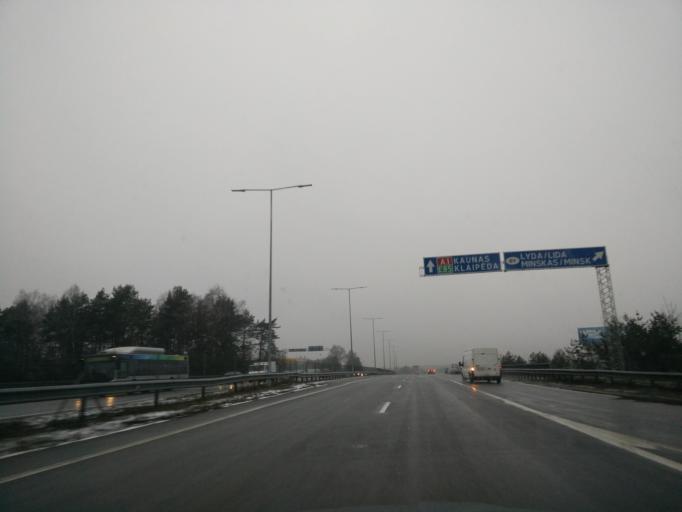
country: LT
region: Vilnius County
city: Pilaite
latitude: 54.6543
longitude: 25.1520
